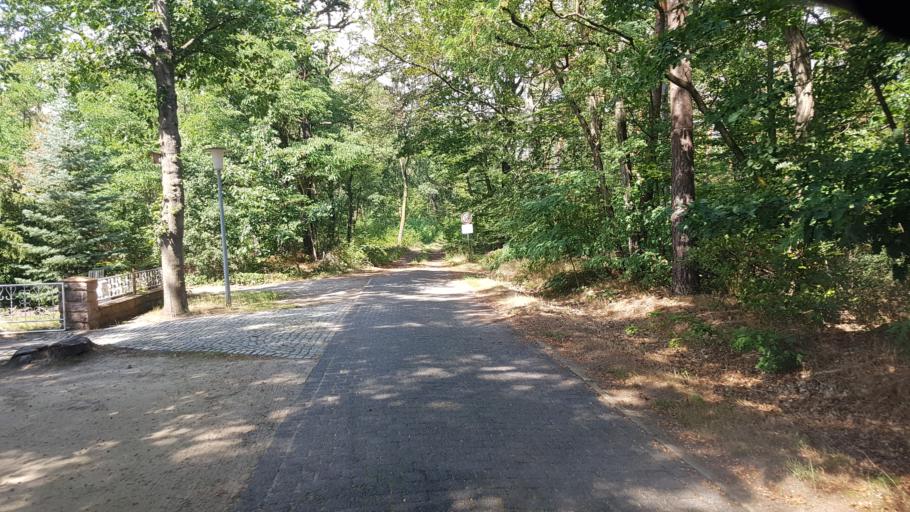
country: DE
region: Brandenburg
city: Calau
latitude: 51.7795
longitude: 13.9545
